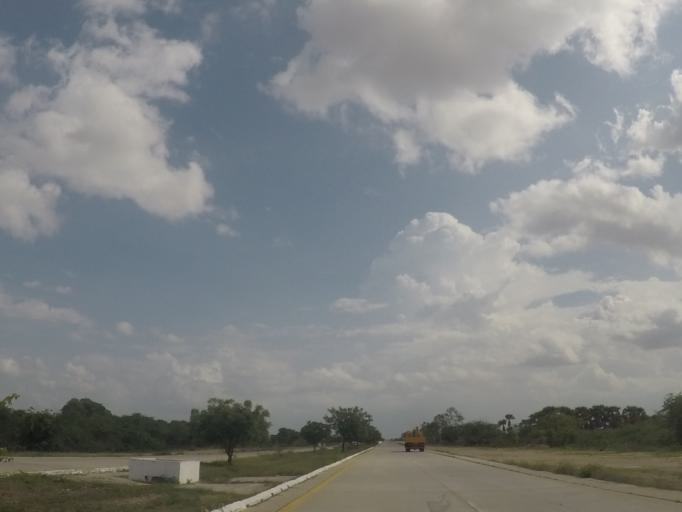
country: MM
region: Mandalay
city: Kyaukse
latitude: 21.3118
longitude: 95.8641
